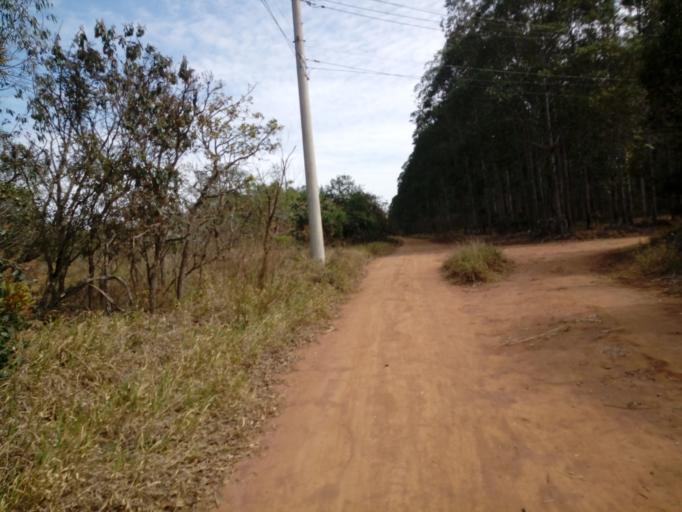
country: BR
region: Sao Paulo
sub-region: Sao Carlos
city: Sao Carlos
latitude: -21.9745
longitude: -47.8748
